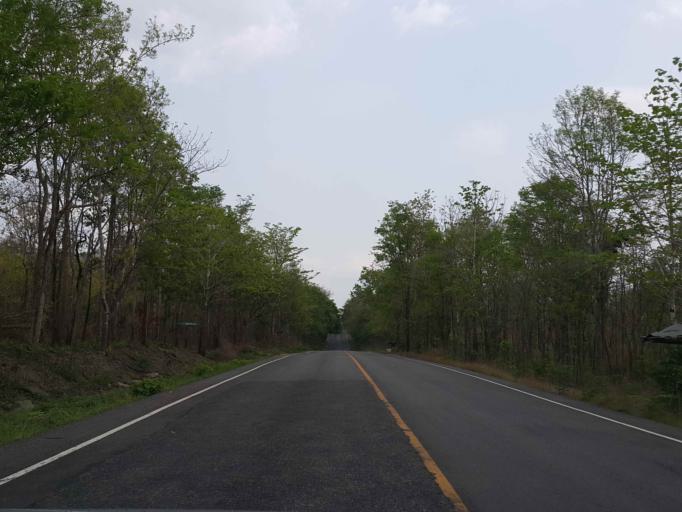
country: TH
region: Sukhothai
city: Thung Saliam
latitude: 17.4147
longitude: 99.3875
